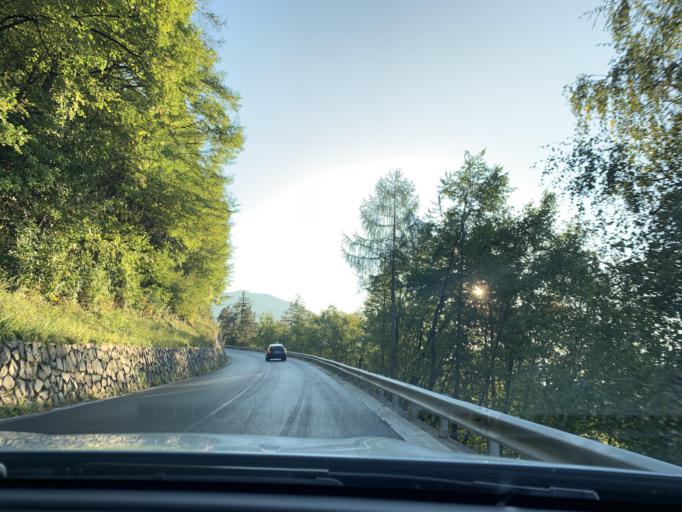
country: IT
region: Trentino-Alto Adige
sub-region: Bolzano
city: Fie Allo Sciliar
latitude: 46.5024
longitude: 11.4712
